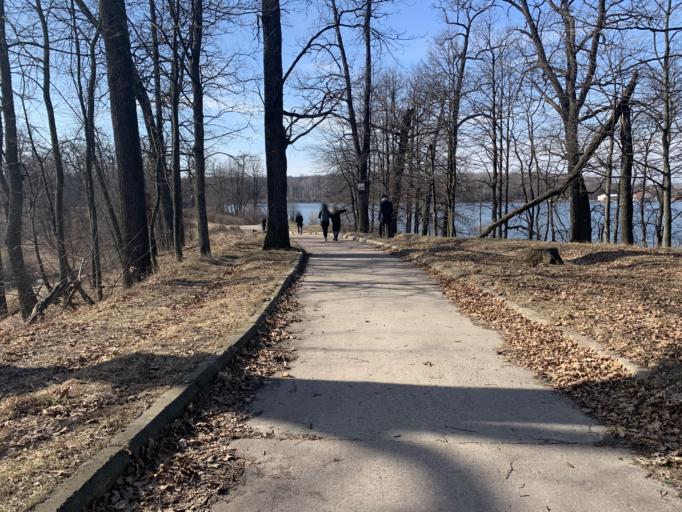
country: RU
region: Kursk
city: Zheleznogorsk
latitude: 52.3188
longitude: 35.3624
